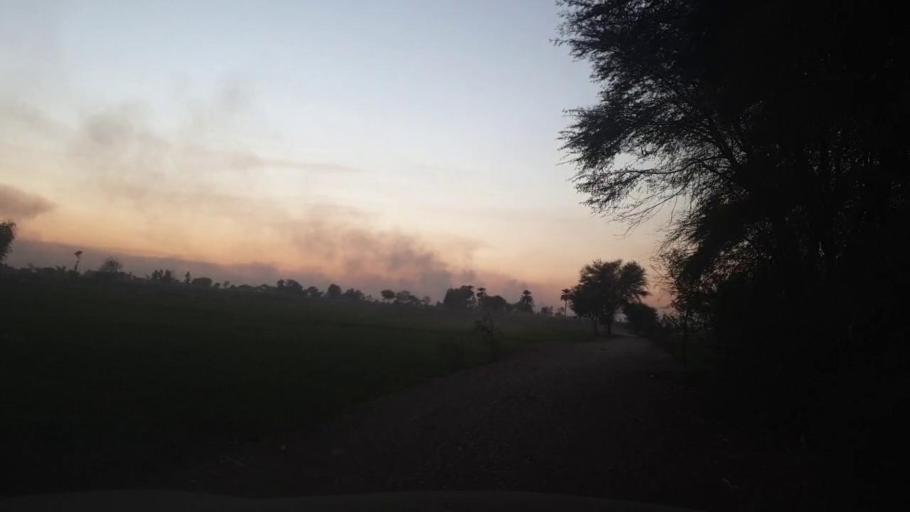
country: PK
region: Sindh
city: Ghotki
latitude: 28.0346
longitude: 69.3511
